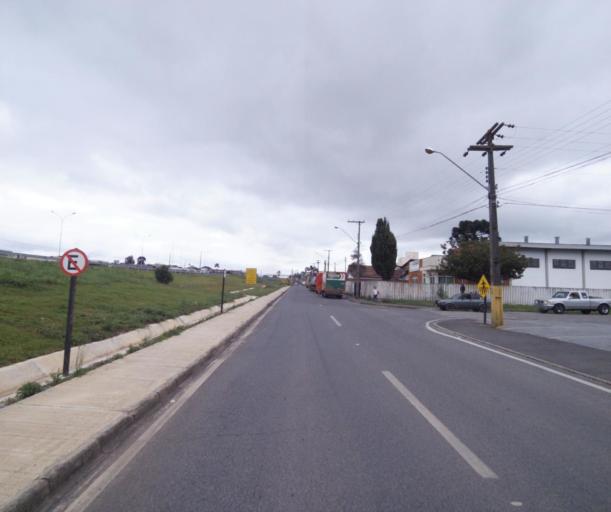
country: BR
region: Parana
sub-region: Quatro Barras
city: Quatro Barras
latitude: -25.3664
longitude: -49.0992
